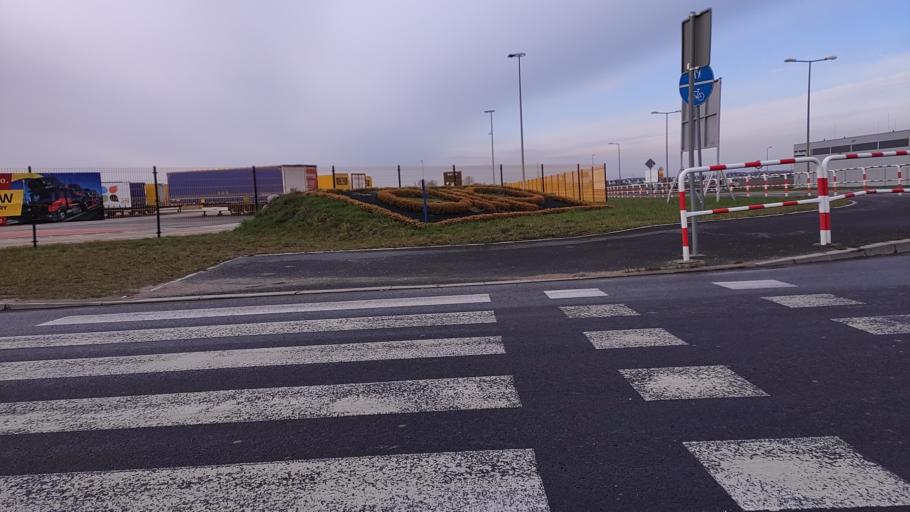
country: PL
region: Greater Poland Voivodeship
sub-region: Powiat poznanski
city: Swarzedz
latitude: 52.3984
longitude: 17.1217
